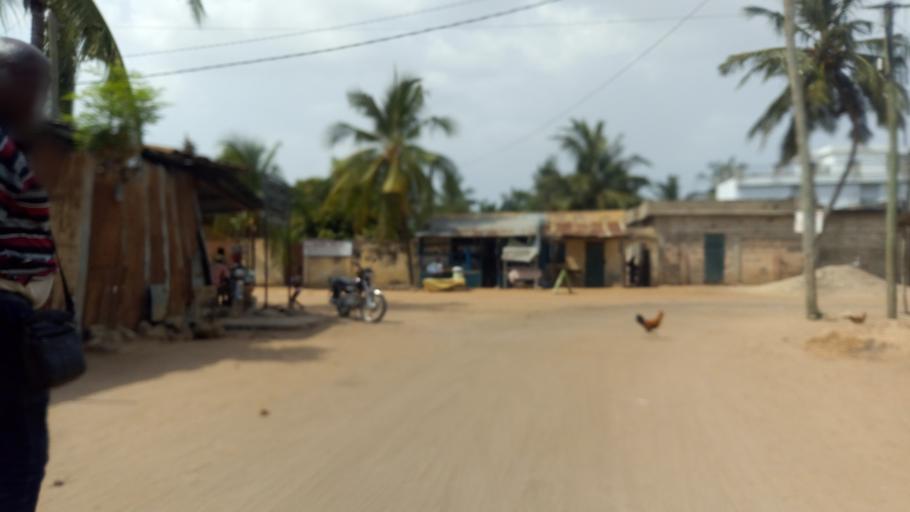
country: TG
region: Maritime
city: Lome
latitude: 6.1779
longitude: 1.1739
